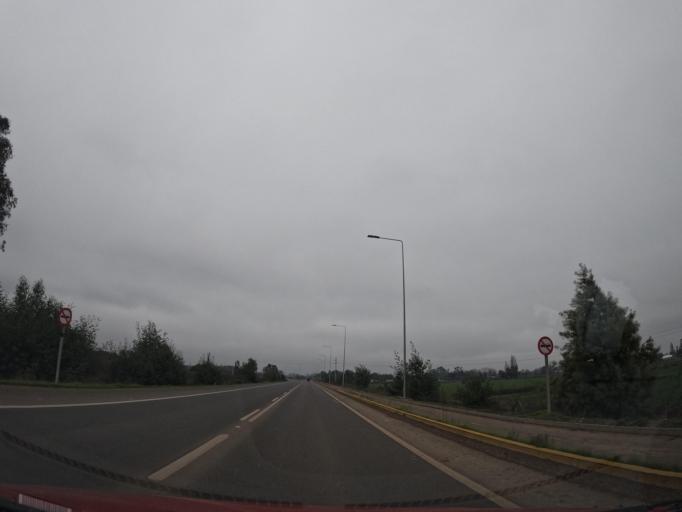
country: CL
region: Maule
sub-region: Provincia de Talca
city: San Clemente
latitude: -35.5252
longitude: -71.4830
